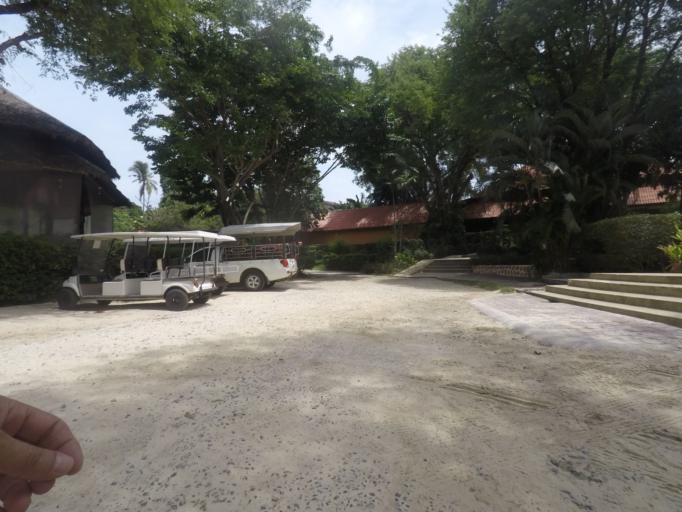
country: TH
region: Phangnga
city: Ban Phru Nai
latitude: 7.7807
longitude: 98.7618
